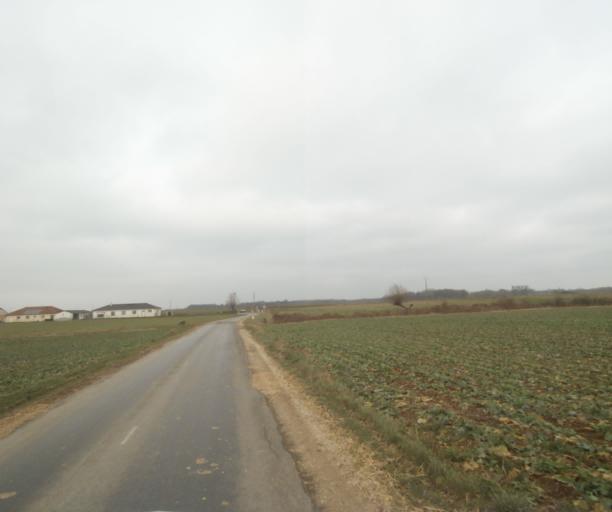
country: FR
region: Champagne-Ardenne
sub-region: Departement de la Haute-Marne
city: Villiers-en-Lieu
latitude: 48.6828
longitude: 4.8422
